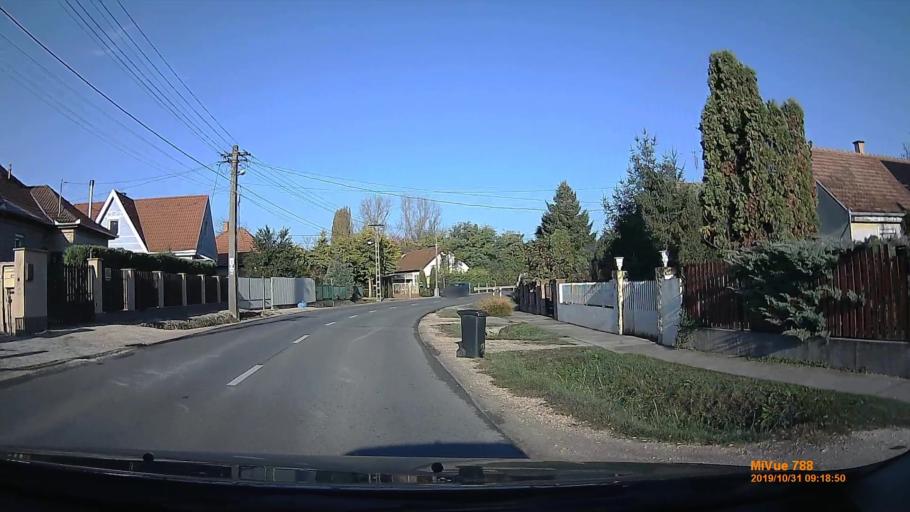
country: HU
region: Pest
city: Gyomro
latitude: 47.4143
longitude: 19.3953
